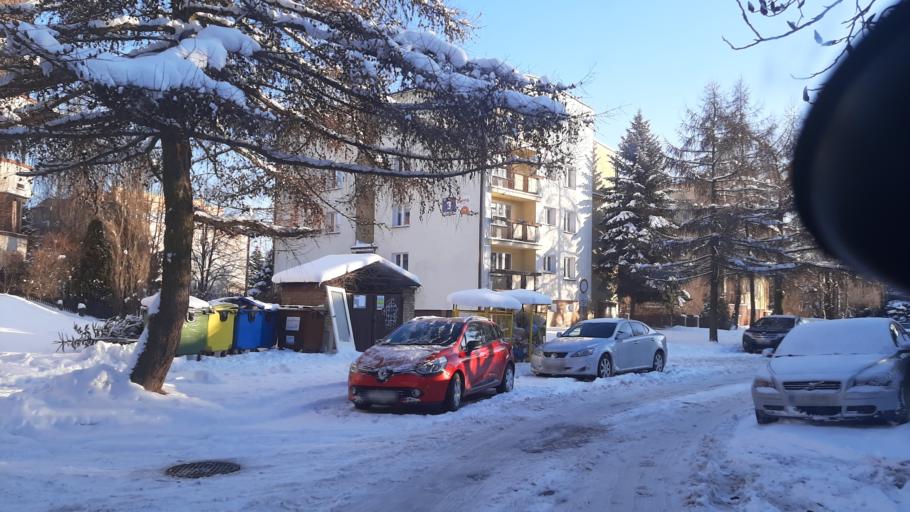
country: PL
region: Lublin Voivodeship
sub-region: Powiat lubelski
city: Lublin
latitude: 51.2789
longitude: 22.5485
